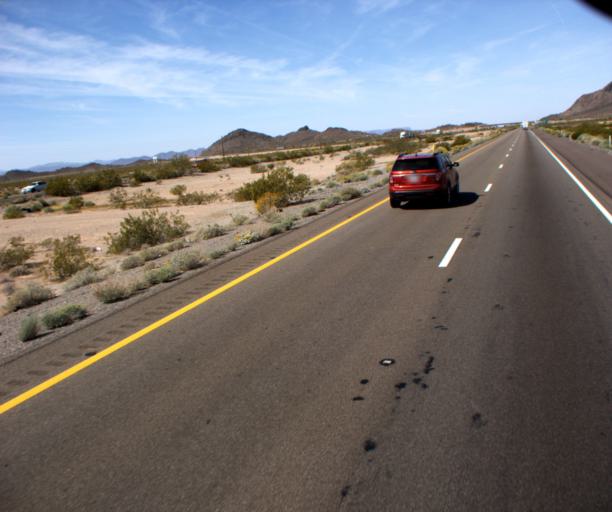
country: US
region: Arizona
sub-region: La Paz County
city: Salome
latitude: 33.6076
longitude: -113.6078
